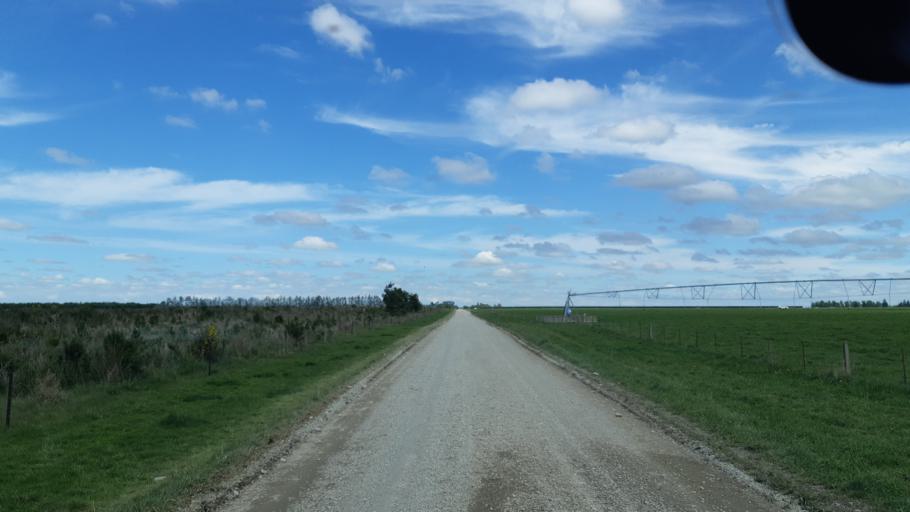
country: NZ
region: Canterbury
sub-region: Ashburton District
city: Methven
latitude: -43.7034
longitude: 171.4601
